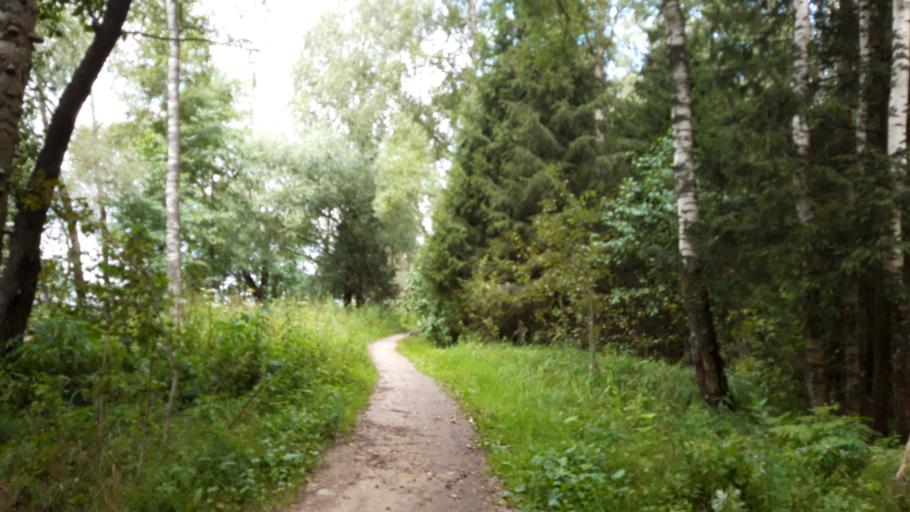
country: RU
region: Tverskaya
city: Konakovo
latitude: 56.6711
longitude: 36.6827
